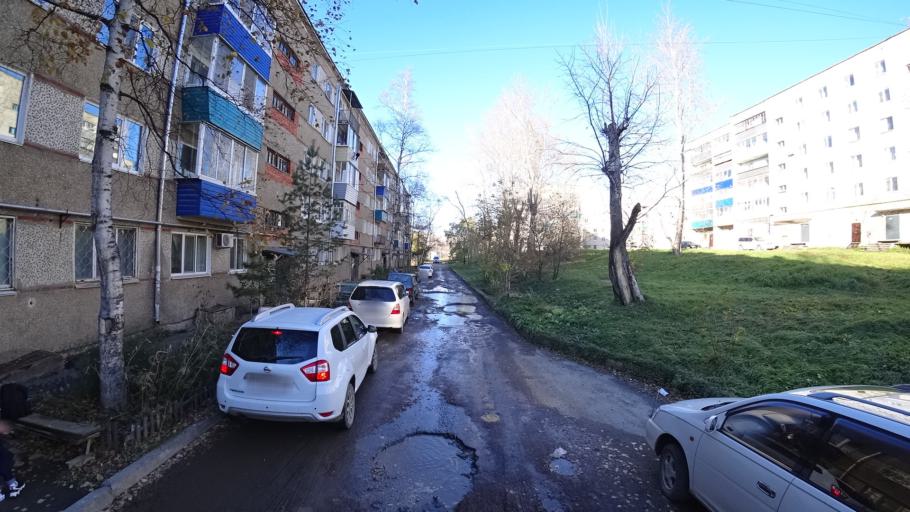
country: RU
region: Khabarovsk Krai
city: Amursk
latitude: 50.2309
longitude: 136.9113
